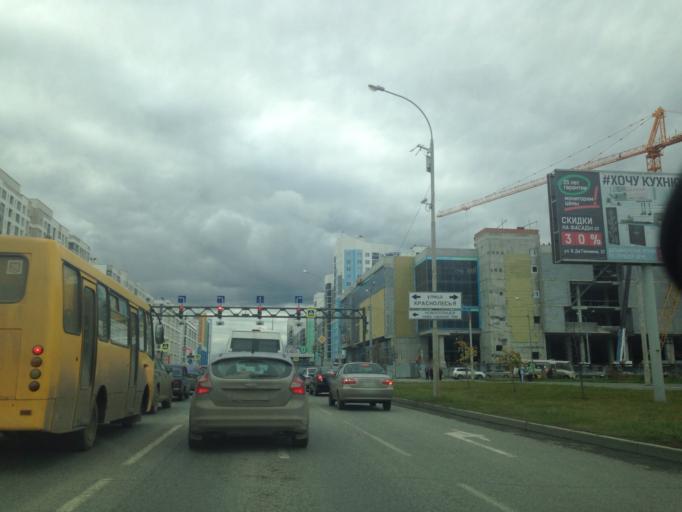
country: RU
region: Sverdlovsk
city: Shirokaya Rechka
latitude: 56.7937
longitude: 60.5224
